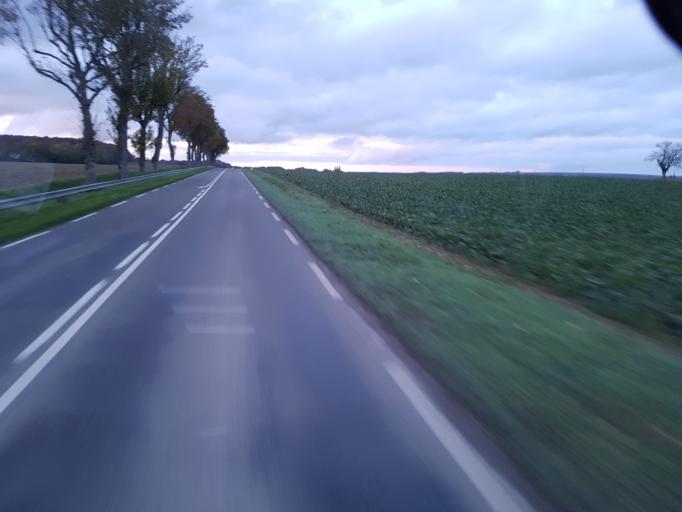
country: FR
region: Picardie
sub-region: Departement de l'Aisne
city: Coincy
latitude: 49.1575
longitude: 3.3846
